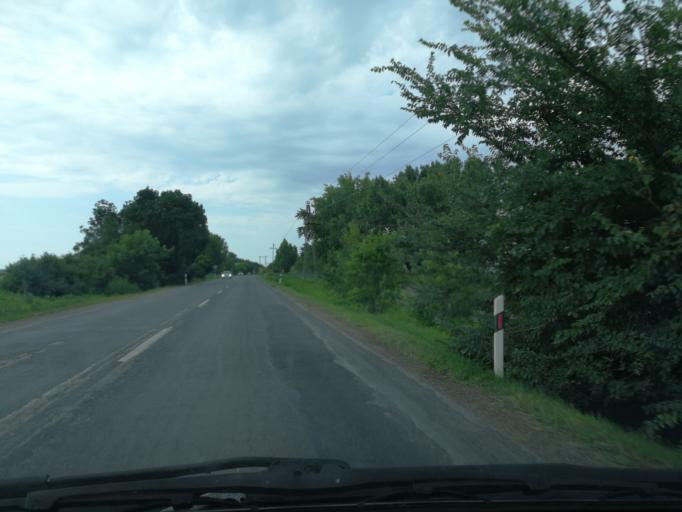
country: HU
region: Bacs-Kiskun
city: Dusnok
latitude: 46.3673
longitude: 18.9632
